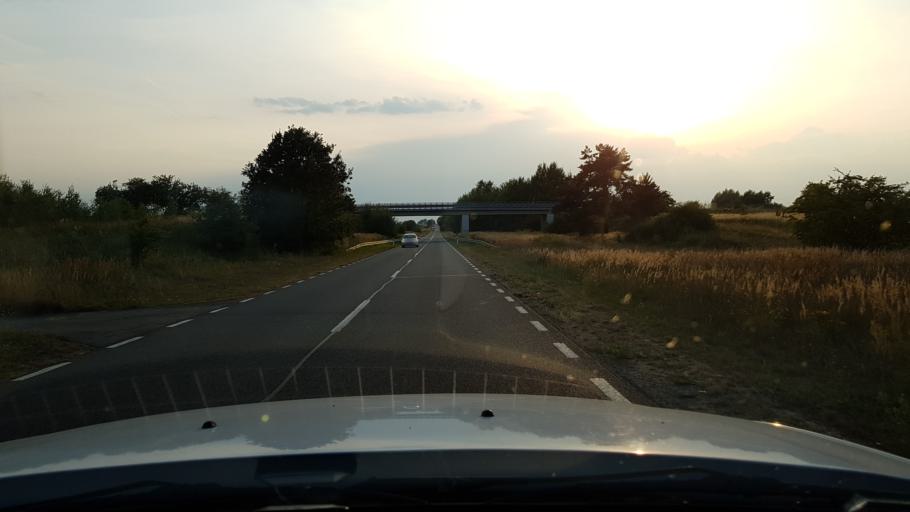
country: PL
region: West Pomeranian Voivodeship
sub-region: Powiat stargardzki
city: Stara Dabrowa
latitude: 53.4343
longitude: 15.1913
